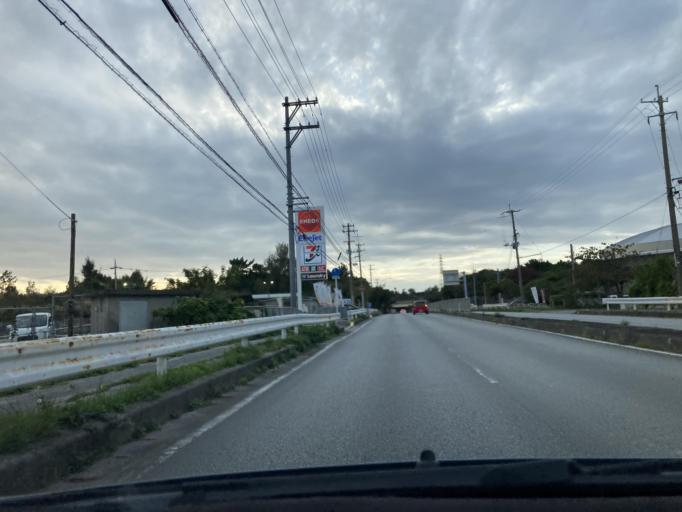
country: JP
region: Okinawa
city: Ishikawa
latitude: 26.4353
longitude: 127.8271
